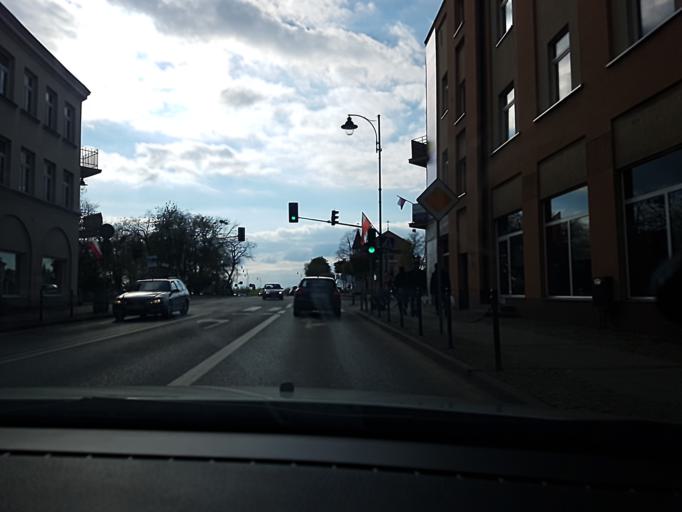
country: PL
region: Masovian Voivodeship
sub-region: Powiat sochaczewski
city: Sochaczew
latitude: 52.2292
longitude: 20.2391
